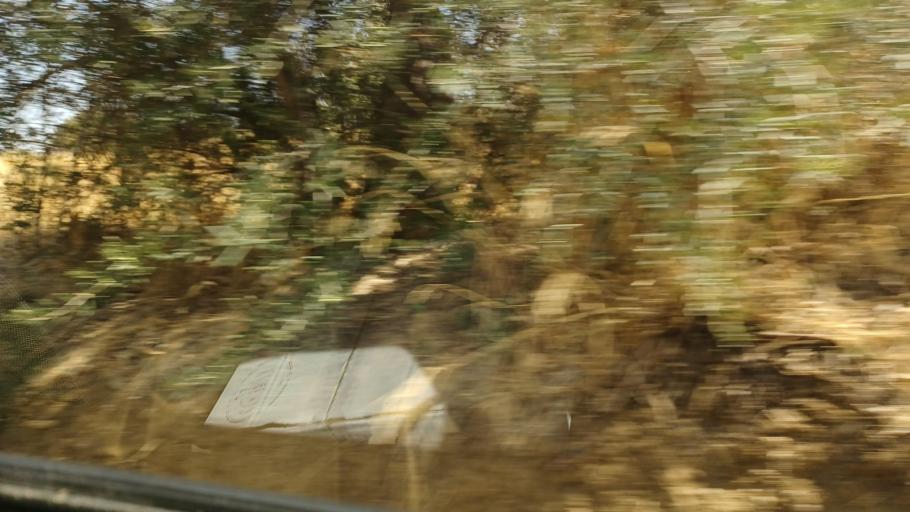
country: CY
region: Lefkosia
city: Lefka
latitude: 35.0622
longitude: 32.8861
